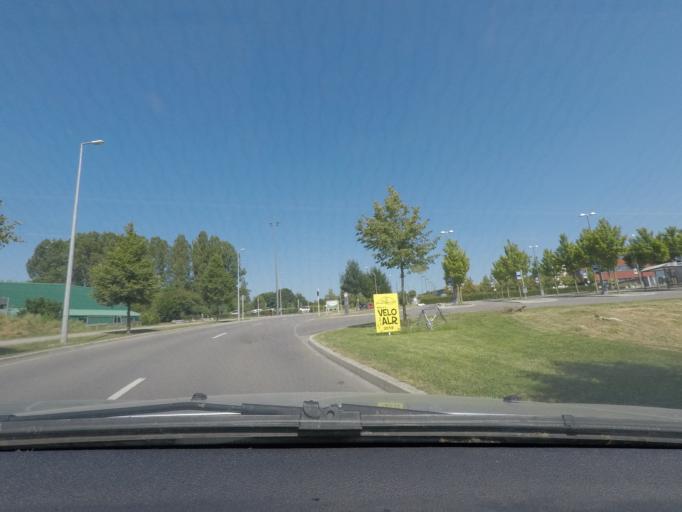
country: LU
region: Diekirch
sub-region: Canton de Redange
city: Redange-sur-Attert
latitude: 49.7688
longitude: 5.8984
